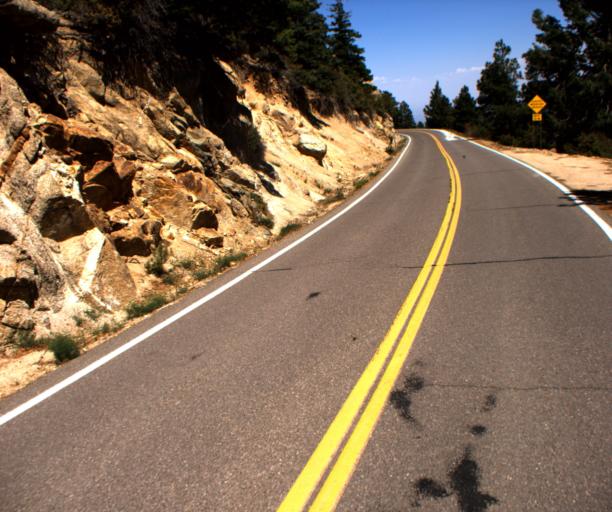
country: US
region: Arizona
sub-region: Graham County
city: Swift Trail Junction
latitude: 32.6210
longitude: -109.8274
